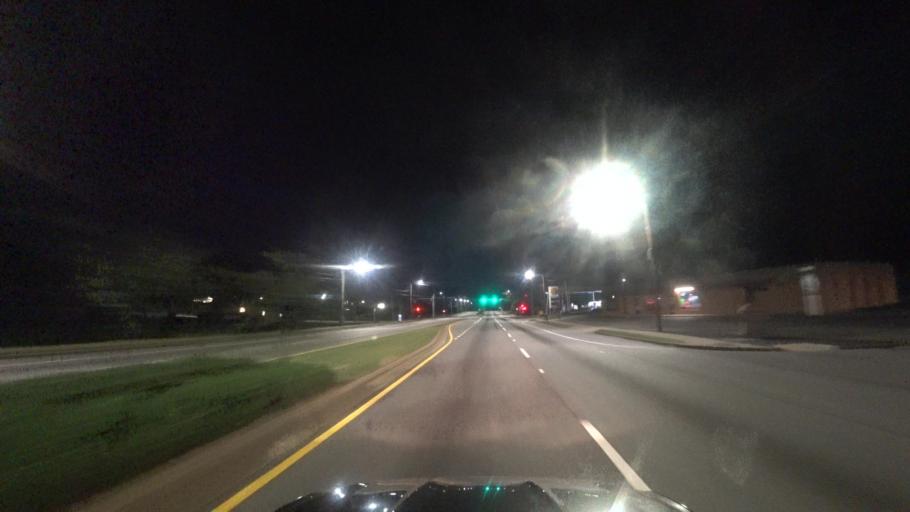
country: US
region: Georgia
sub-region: Clayton County
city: Forest Park
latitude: 33.6184
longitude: -84.3592
